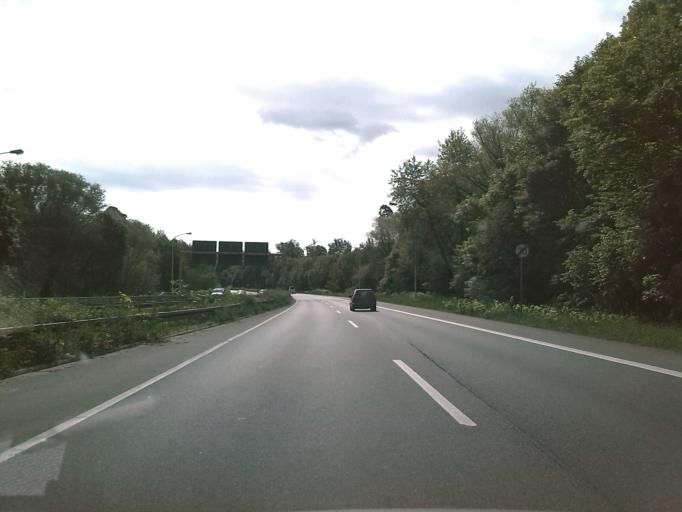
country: DE
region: Hesse
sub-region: Regierungsbezirk Darmstadt
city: Darmstadt
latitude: 49.8673
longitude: 8.6883
